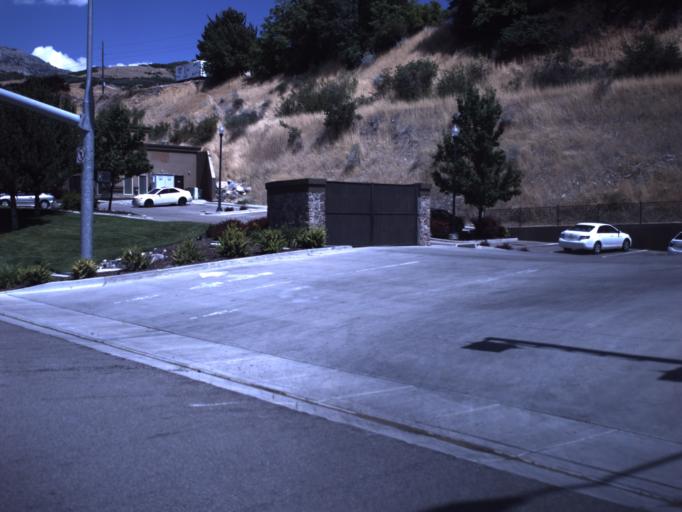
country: US
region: Utah
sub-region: Utah County
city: Orem
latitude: 40.3027
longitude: -111.6558
